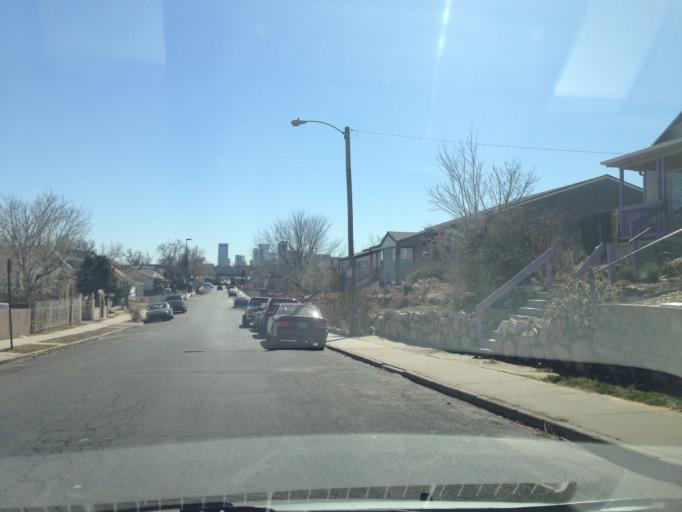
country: US
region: Colorado
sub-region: Denver County
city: Denver
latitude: 39.7832
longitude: -104.9859
